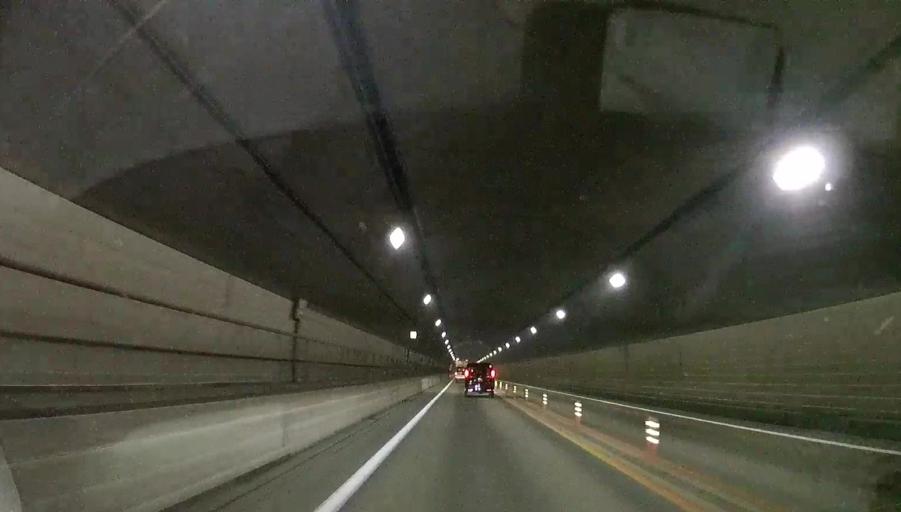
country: JP
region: Hokkaido
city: Shimo-furano
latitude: 43.0419
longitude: 142.4755
